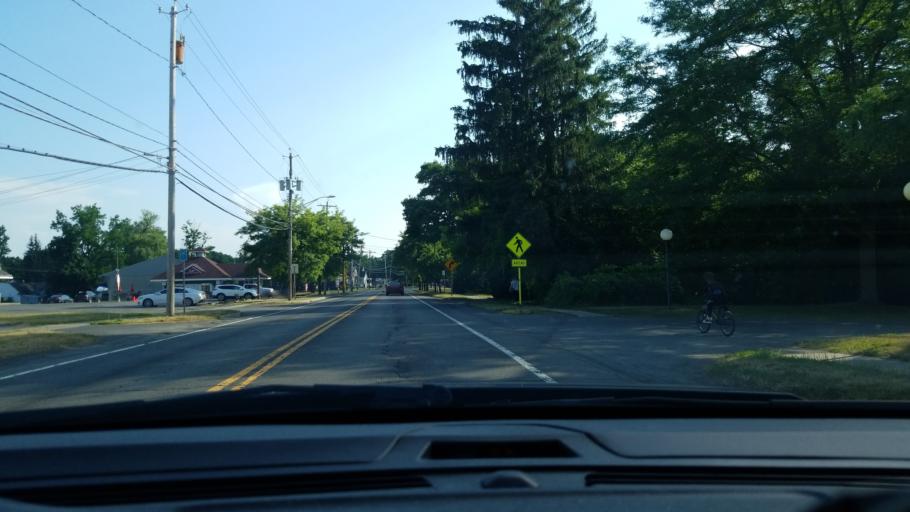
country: US
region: New York
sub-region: Onondaga County
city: North Syracuse
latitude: 43.1287
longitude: -76.1347
